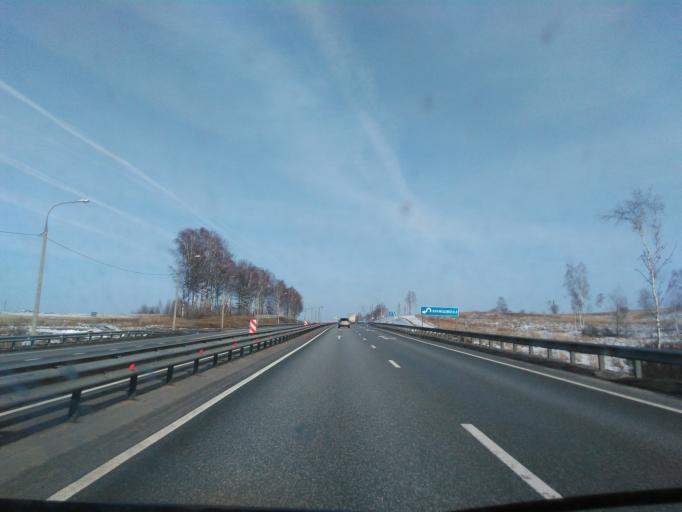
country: RU
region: Smolensk
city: Verkhnedneprovskiy
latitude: 55.1719
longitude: 33.4293
